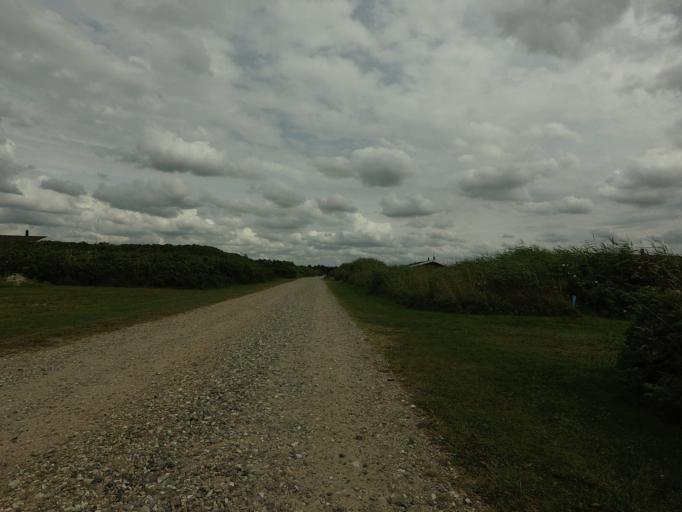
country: DK
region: North Denmark
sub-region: Jammerbugt Kommune
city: Pandrup
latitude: 57.3579
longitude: 9.6990
